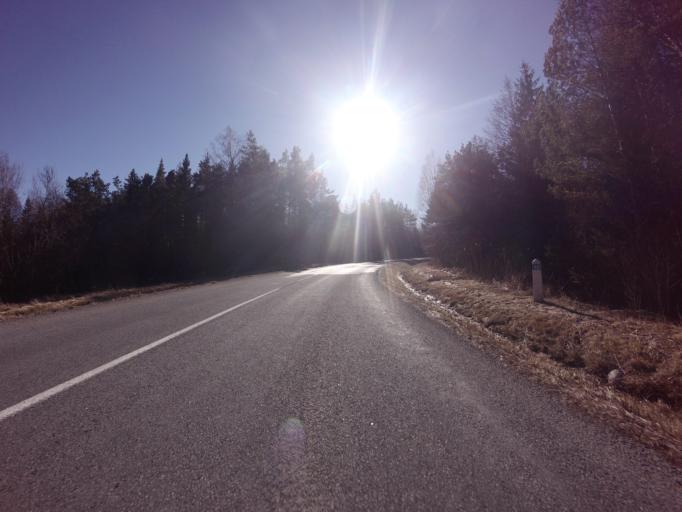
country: EE
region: Saare
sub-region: Kuressaare linn
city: Kuressaare
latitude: 58.5048
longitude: 22.3114
